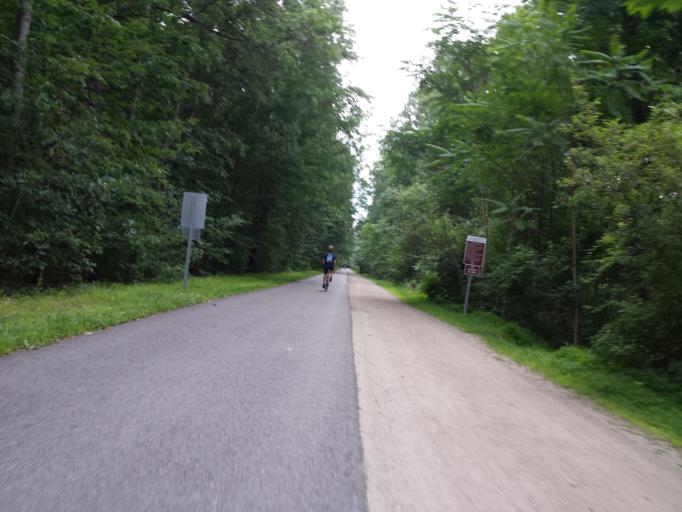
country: US
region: New York
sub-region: Dutchess County
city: Hillside Lake
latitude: 41.5899
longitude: -73.8244
